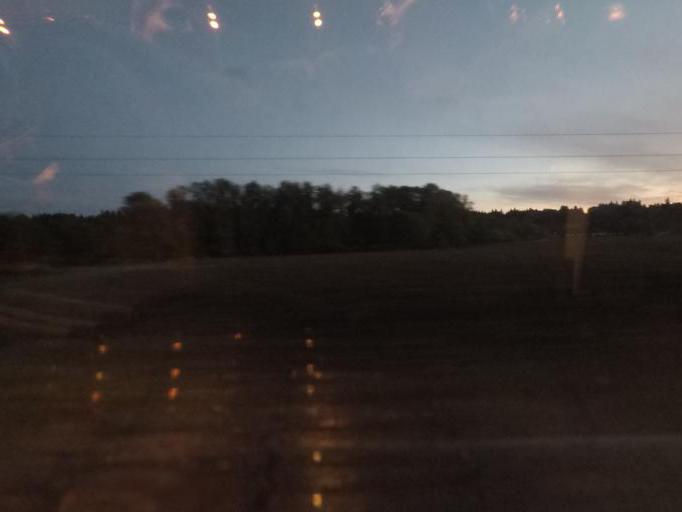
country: US
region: Washington
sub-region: Snohomish County
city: Smokey Point
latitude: 48.1969
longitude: -122.2457
